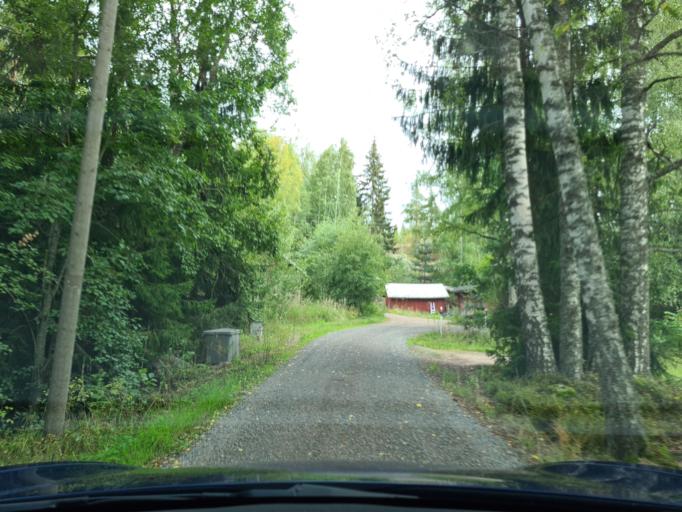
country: FI
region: Uusimaa
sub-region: Helsinki
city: Vihti
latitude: 60.4172
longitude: 24.4973
